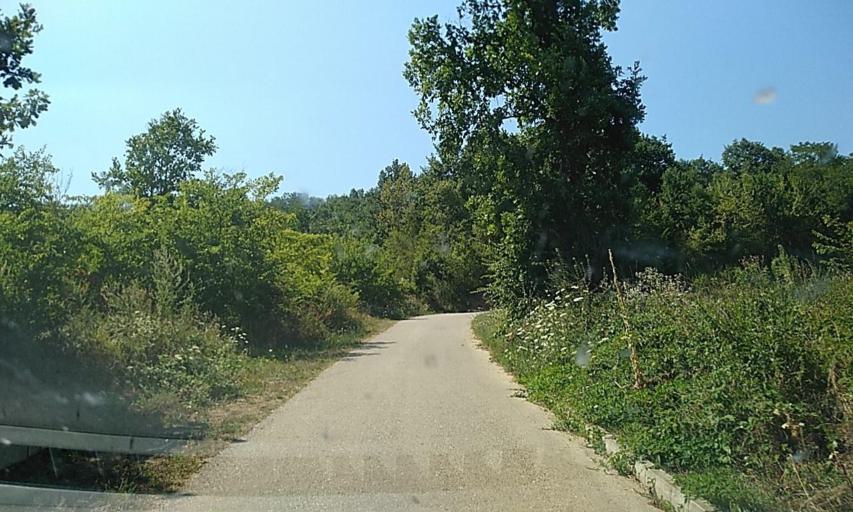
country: RS
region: Central Serbia
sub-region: Pcinjski Okrug
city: Vladicin Han
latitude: 42.7536
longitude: 22.0756
